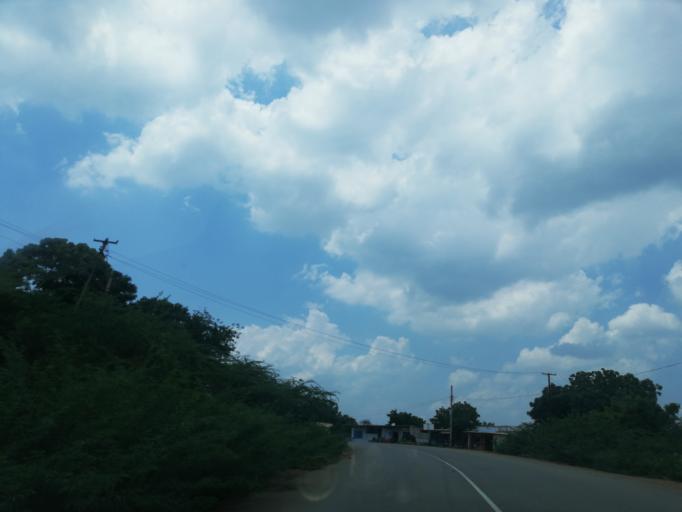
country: IN
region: Andhra Pradesh
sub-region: Guntur
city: Macherla
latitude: 16.5854
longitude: 79.3264
